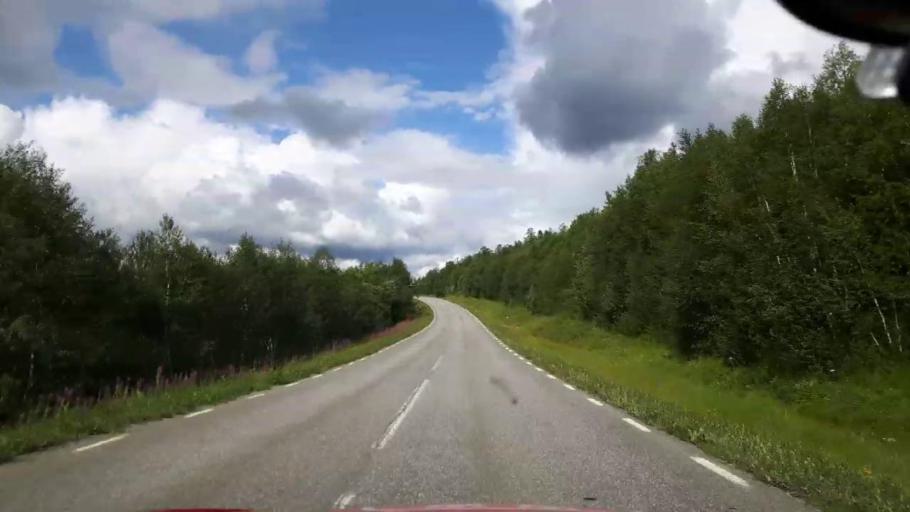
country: NO
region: Nordland
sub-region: Hattfjelldal
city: Hattfjelldal
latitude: 65.0525
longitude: 14.7385
